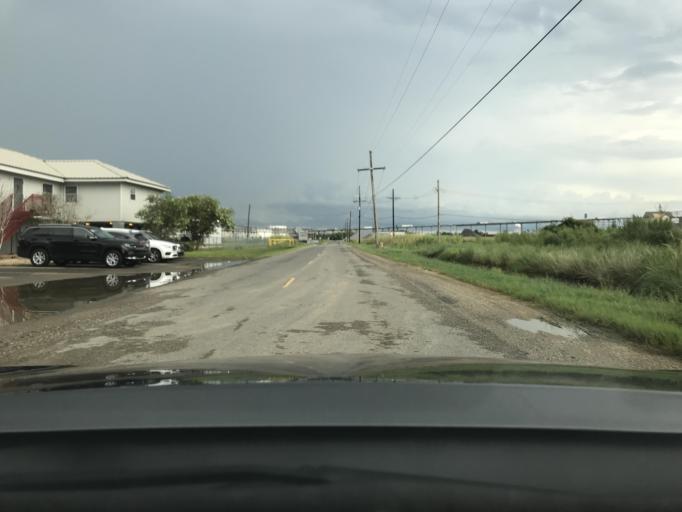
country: US
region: Louisiana
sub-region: Calcasieu Parish
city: Westlake
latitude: 30.2268
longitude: -93.2513
